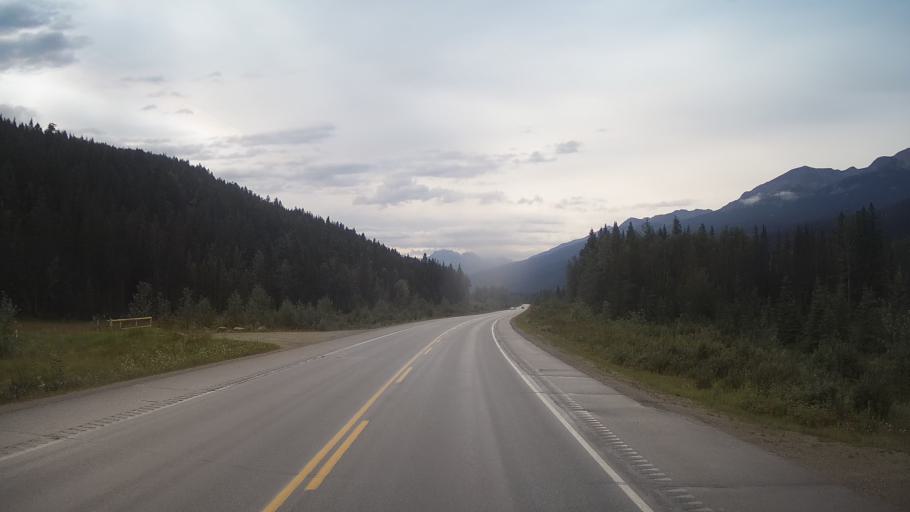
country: CA
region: Alberta
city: Jasper Park Lodge
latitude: 52.9182
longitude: -118.7981
